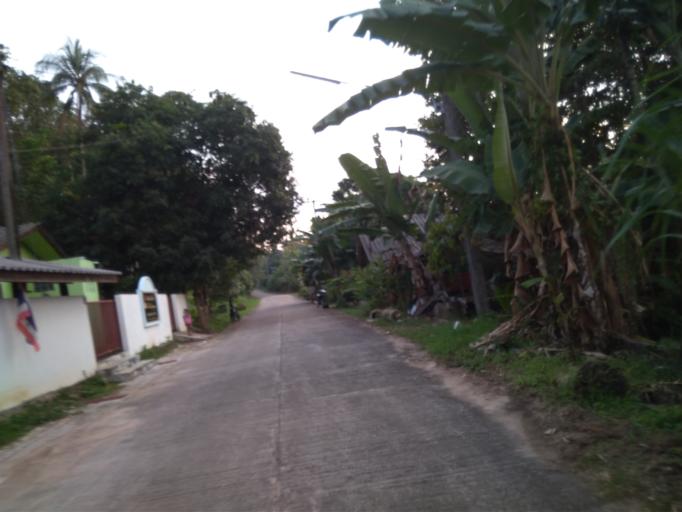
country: TH
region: Phangnga
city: Ko Yao
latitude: 8.1475
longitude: 98.5990
